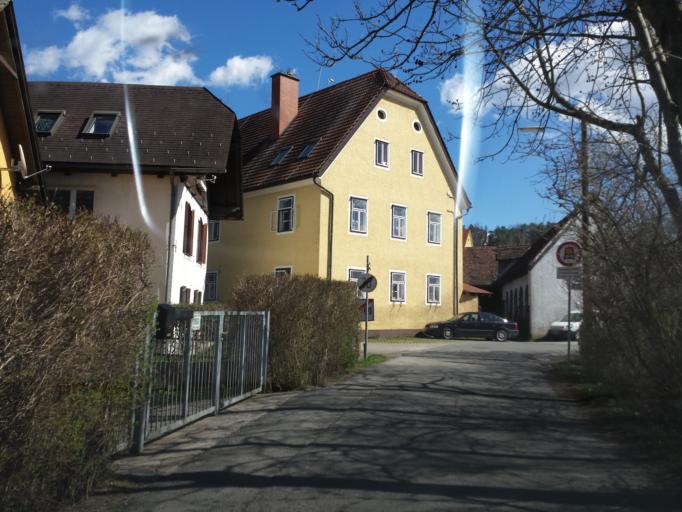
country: AT
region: Styria
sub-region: Politischer Bezirk Graz-Umgebung
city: Stattegg
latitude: 47.1258
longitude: 15.4270
